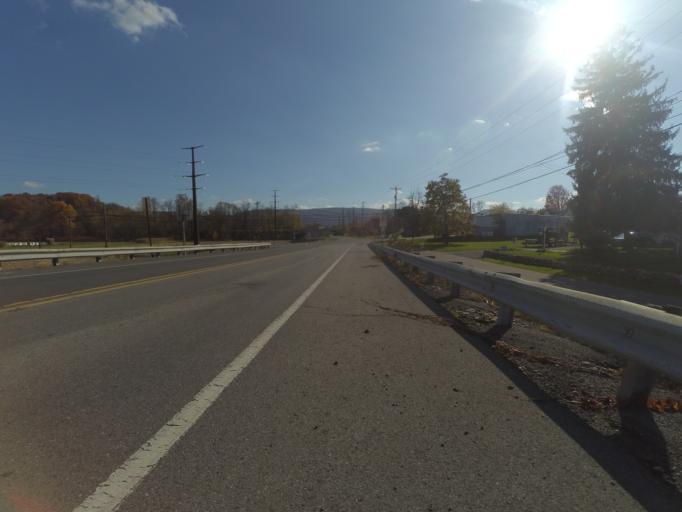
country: US
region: Pennsylvania
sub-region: Clinton County
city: Avis
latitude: 41.1950
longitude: -77.2967
